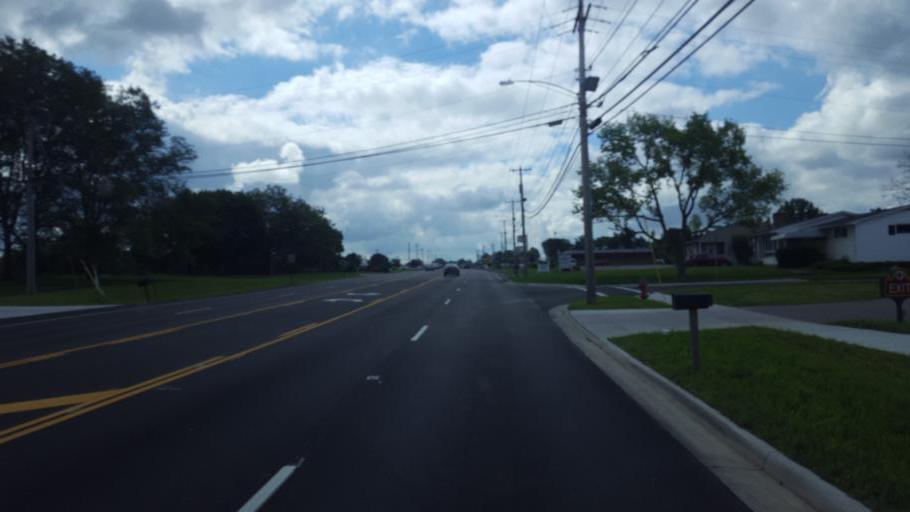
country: US
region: Ohio
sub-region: Richland County
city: Shelby
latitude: 40.8699
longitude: -82.6457
